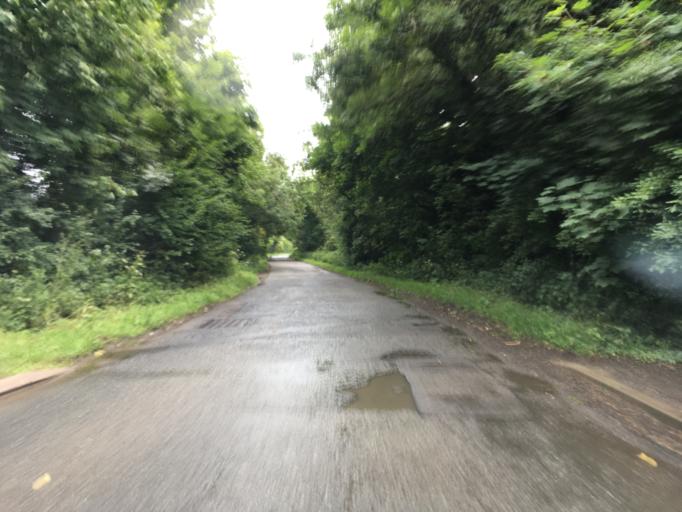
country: GB
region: England
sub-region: Northamptonshire
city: Daventry
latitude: 52.2443
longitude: -1.2066
